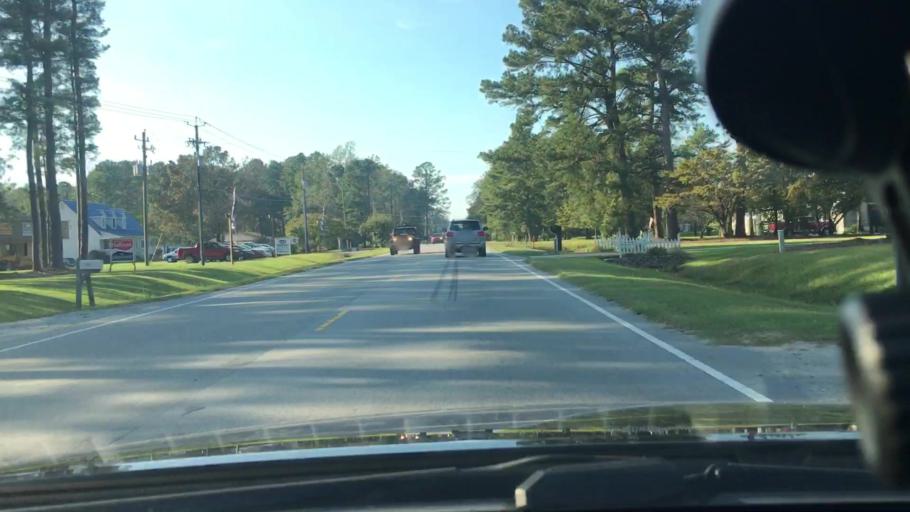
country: US
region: North Carolina
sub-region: Craven County
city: Vanceboro
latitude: 35.2524
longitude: -77.0919
